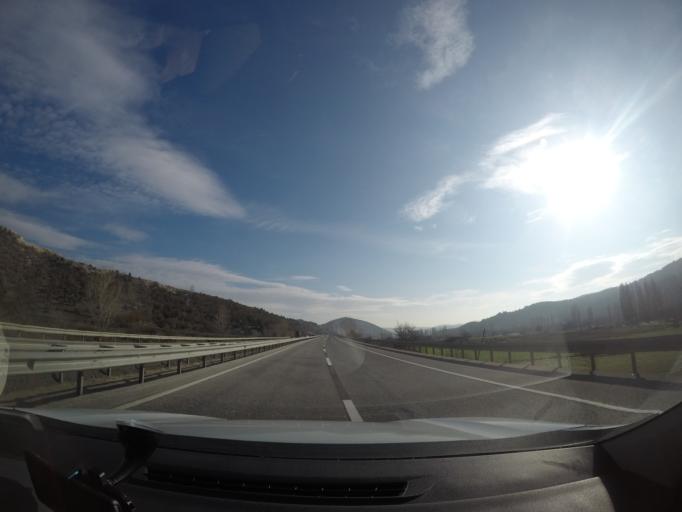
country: TR
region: Bilecik
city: Bozuyuk
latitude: 39.8934
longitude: 29.9503
